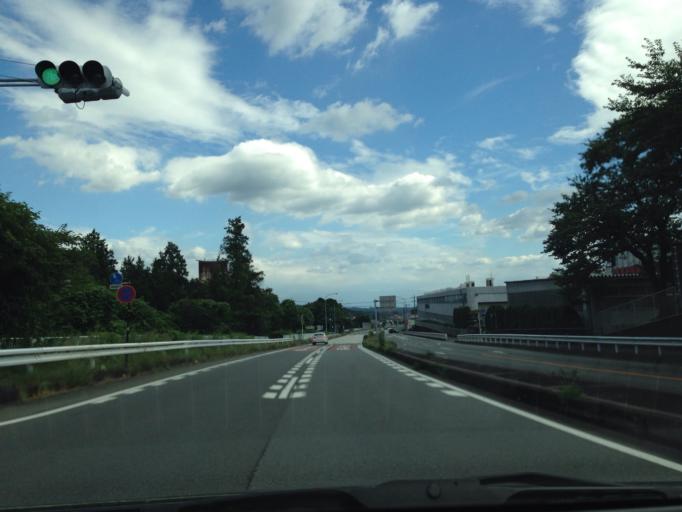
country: JP
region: Shizuoka
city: Gotemba
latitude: 35.2165
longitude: 138.9168
